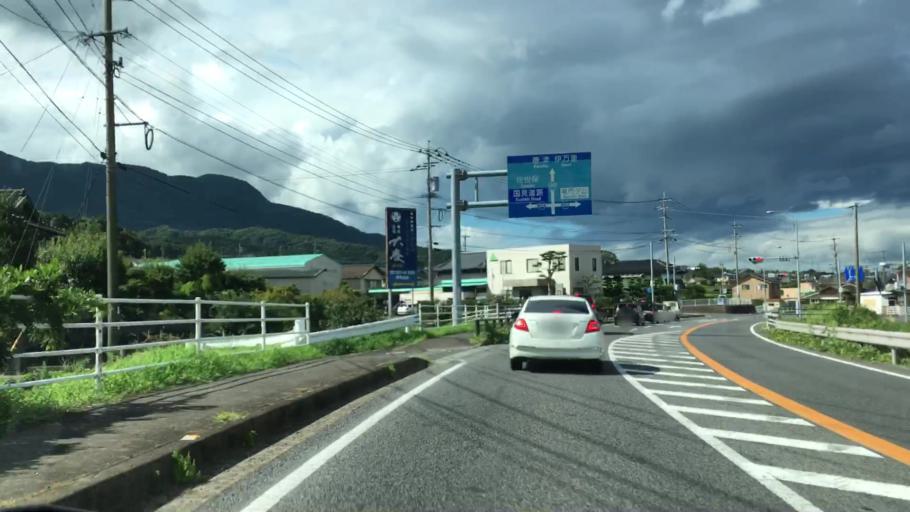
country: JP
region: Saga Prefecture
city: Imaricho-ko
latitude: 33.2246
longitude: 129.8471
